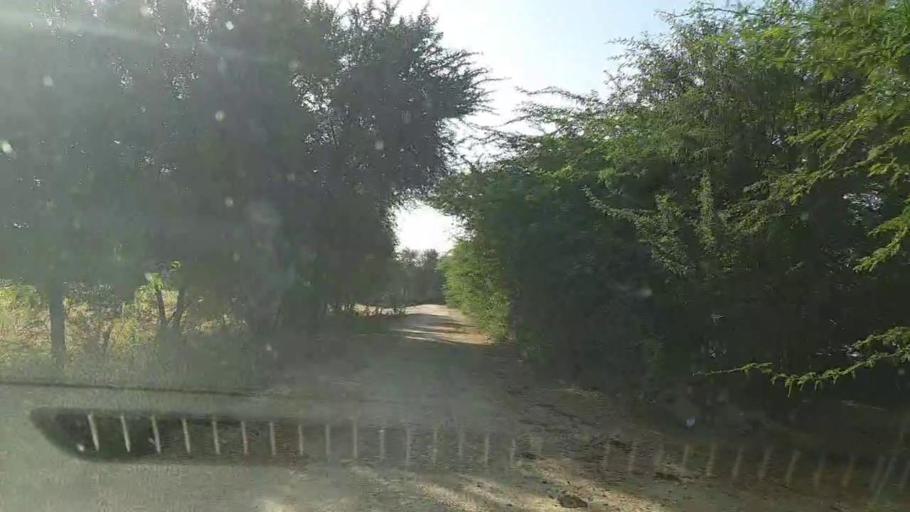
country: PK
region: Sindh
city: Kotri
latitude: 25.1397
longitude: 68.2909
